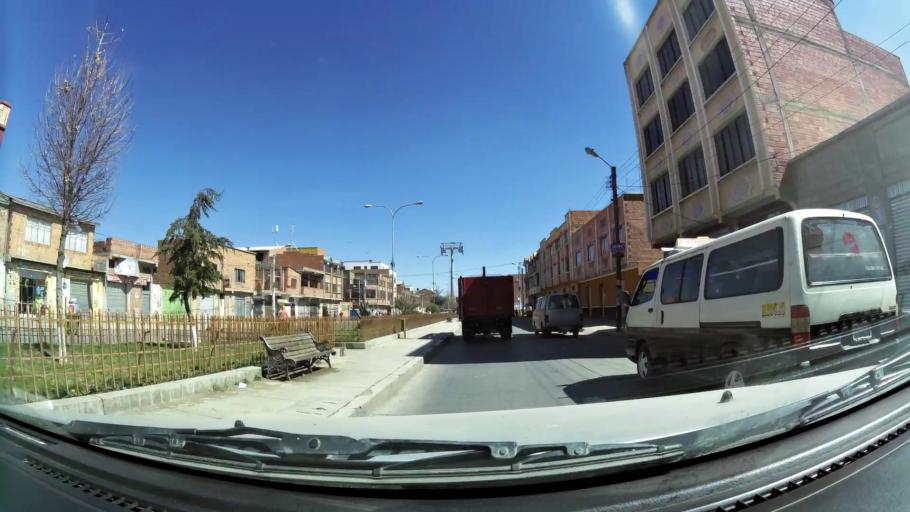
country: BO
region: La Paz
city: La Paz
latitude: -16.4905
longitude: -68.1897
